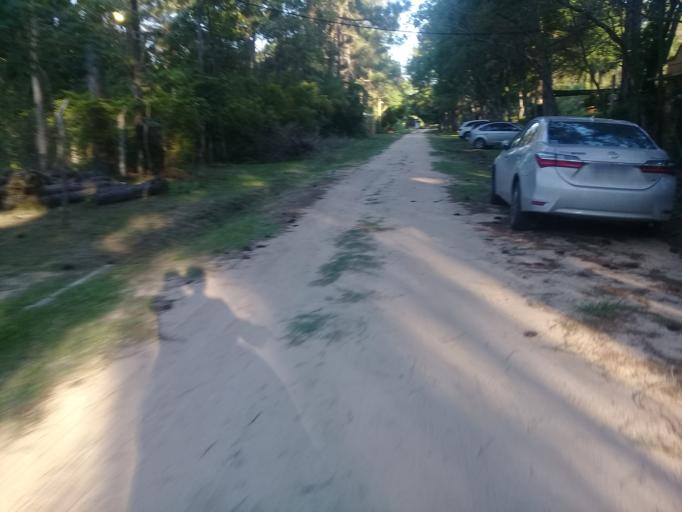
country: AR
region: Corrientes
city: San Luis del Palmar
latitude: -27.4652
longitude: -58.6645
